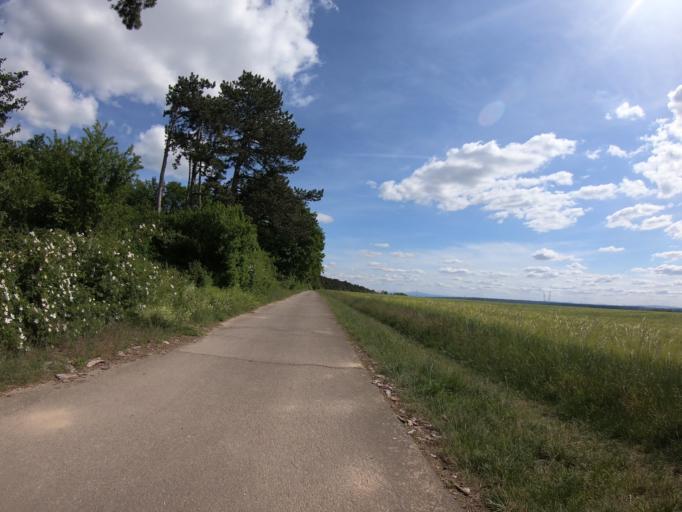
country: DE
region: Lower Saxony
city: Leiferde
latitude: 52.1917
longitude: 10.5261
